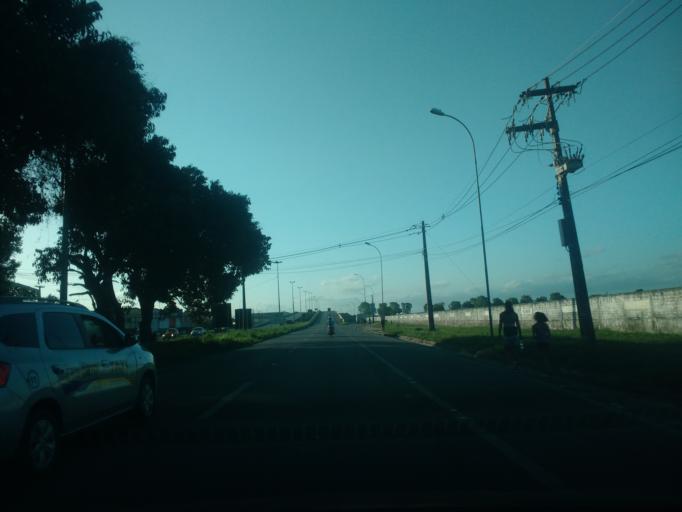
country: BR
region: Alagoas
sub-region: Satuba
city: Satuba
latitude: -9.5173
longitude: -35.8034
